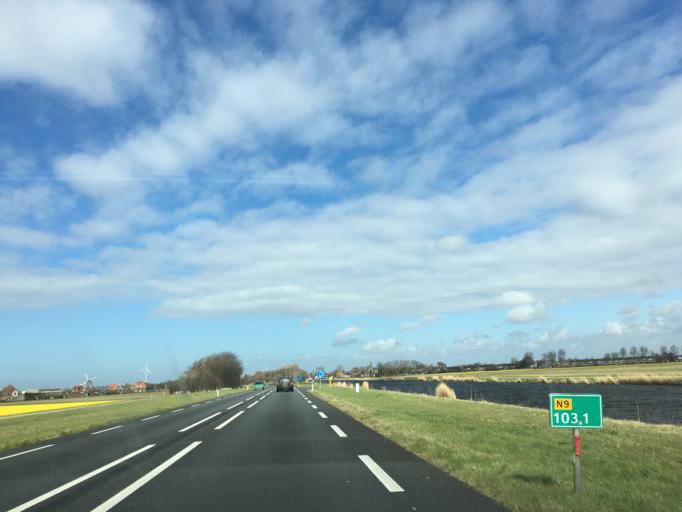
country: NL
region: North Holland
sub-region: Gemeente Schagen
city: Schagen
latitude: 52.8282
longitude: 4.7479
